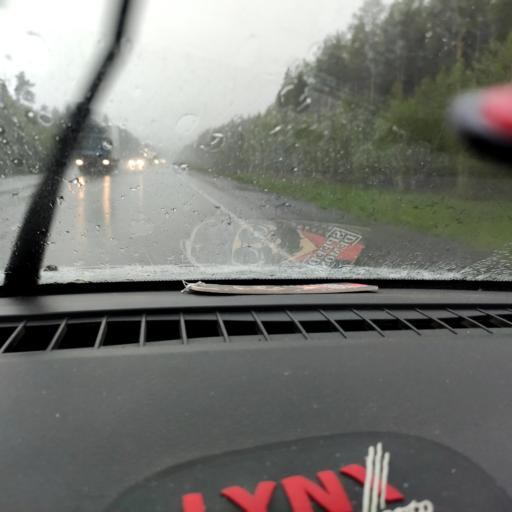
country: RU
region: Sverdlovsk
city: Achit
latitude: 56.8025
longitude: 57.8448
